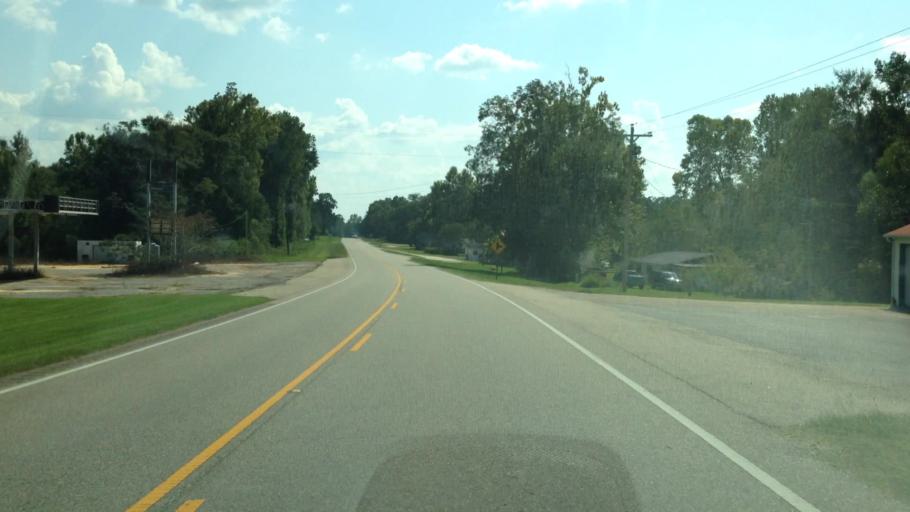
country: US
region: Florida
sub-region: Okaloosa County
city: Crestview
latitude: 31.0307
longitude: -86.6091
